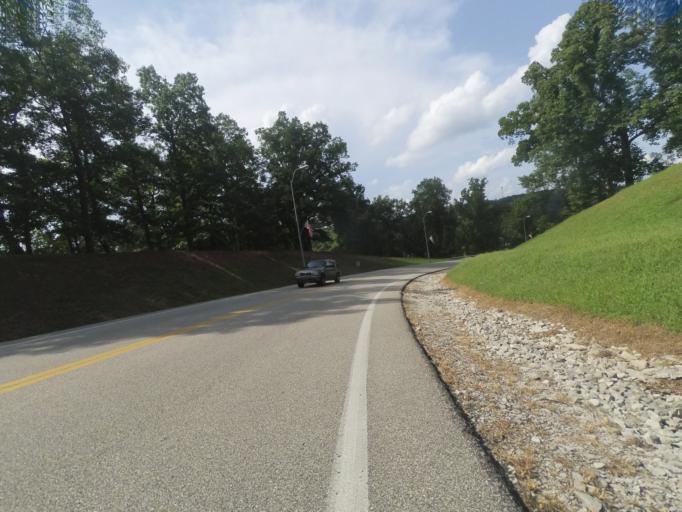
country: US
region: Ohio
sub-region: Lawrence County
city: Burlington
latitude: 38.3801
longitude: -82.5180
